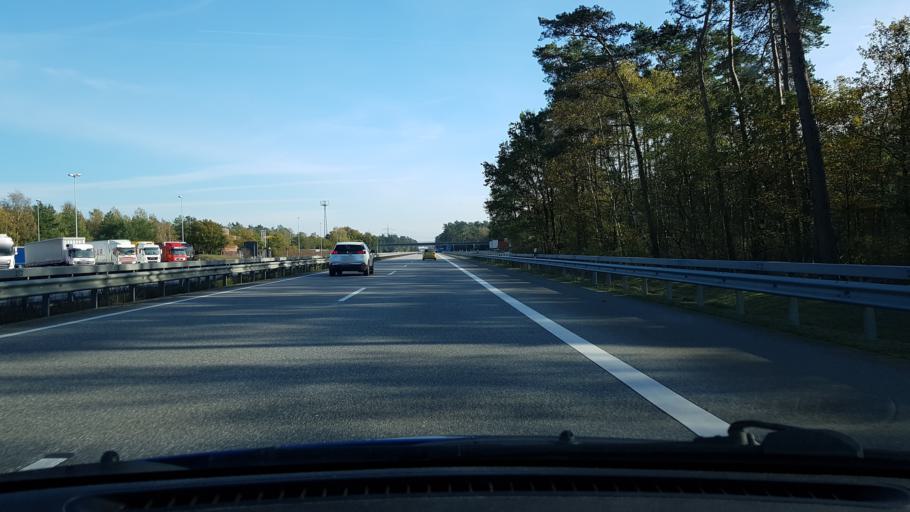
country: DE
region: Schleswig-Holstein
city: Gudow
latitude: 53.5202
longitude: 10.8062
